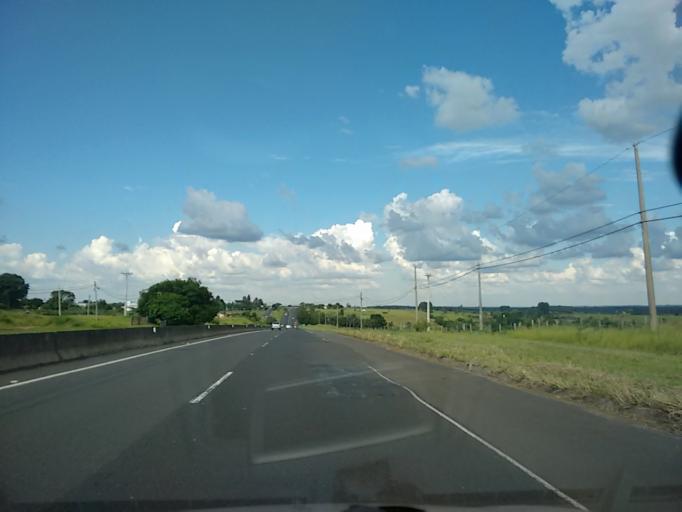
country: BR
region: Sao Paulo
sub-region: Marilia
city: Marilia
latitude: -22.2248
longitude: -49.8901
